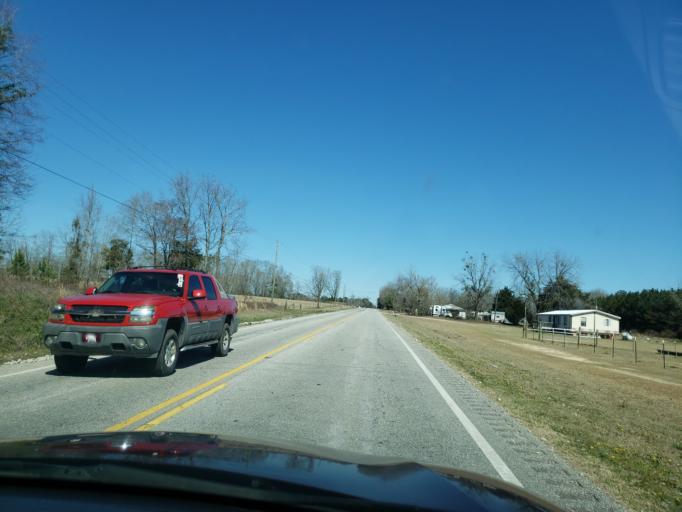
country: US
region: Alabama
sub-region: Macon County
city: Tuskegee
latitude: 32.5749
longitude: -85.6573
